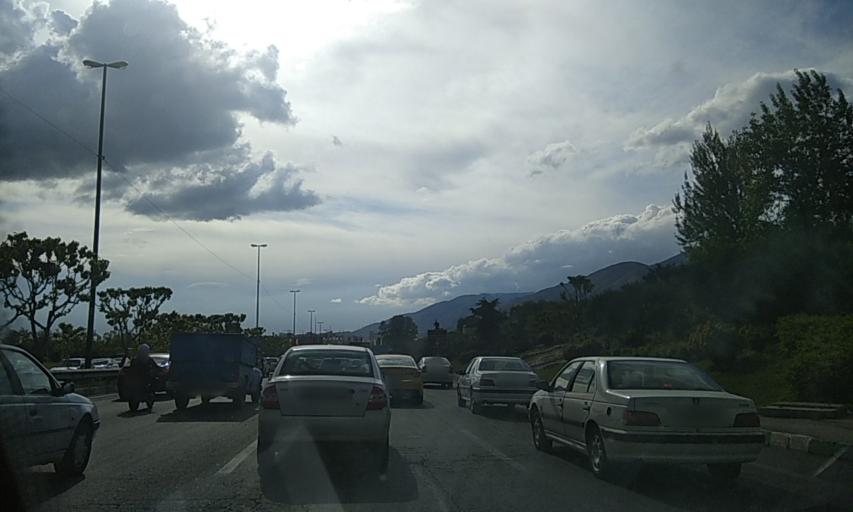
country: IR
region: Tehran
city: Tehran
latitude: 35.7538
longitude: 51.2835
